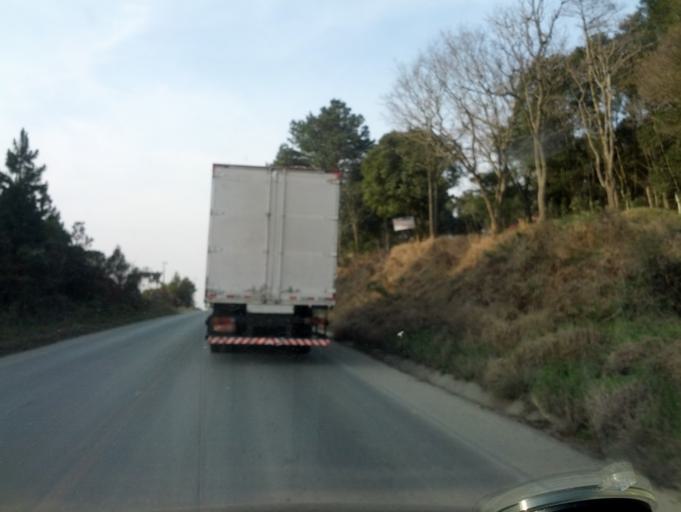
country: BR
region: Santa Catarina
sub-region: Otacilio Costa
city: Otacilio Costa
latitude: -27.5257
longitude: -50.1378
